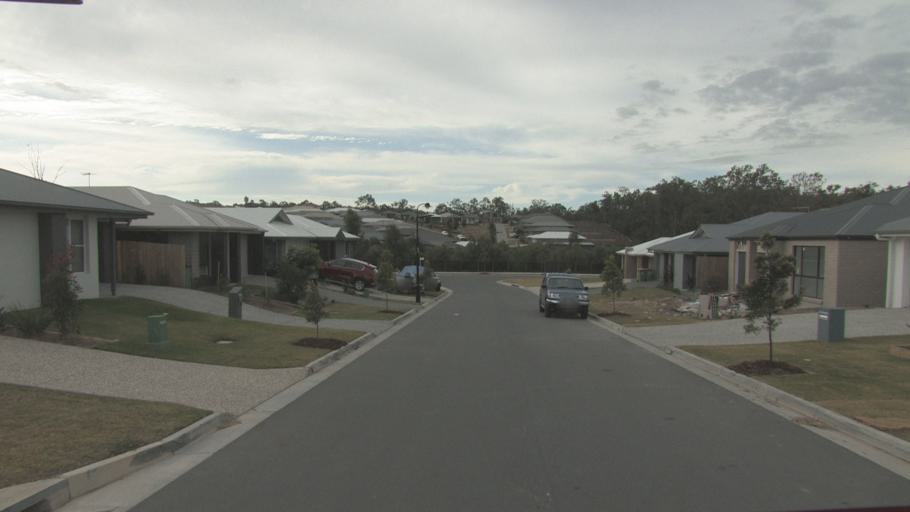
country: AU
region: Queensland
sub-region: Logan
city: Windaroo
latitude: -27.7191
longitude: 153.1659
